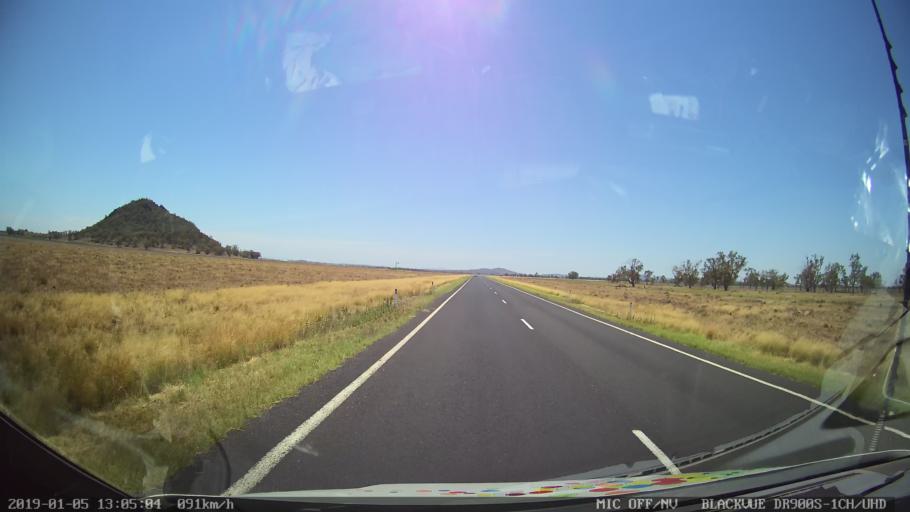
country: AU
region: New South Wales
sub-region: Gunnedah
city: Gunnedah
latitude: -31.0982
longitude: 149.8483
